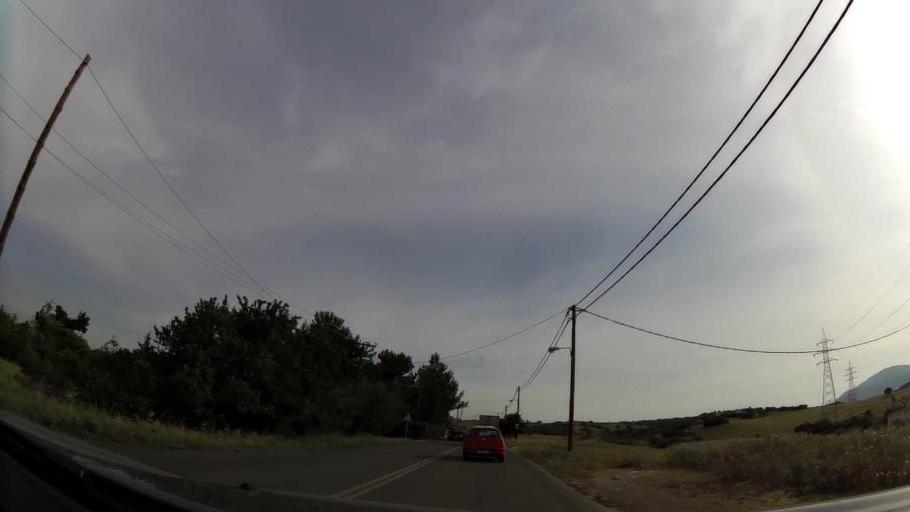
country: GR
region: Central Macedonia
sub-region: Nomos Thessalonikis
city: Thermi
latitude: 40.5642
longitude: 23.0247
